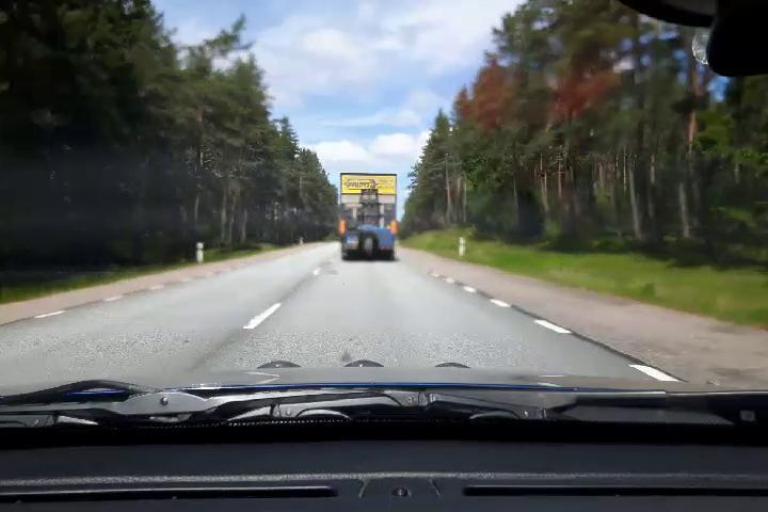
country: SE
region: Uppsala
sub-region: Tierps Kommun
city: Tierp
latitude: 60.1937
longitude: 17.4794
